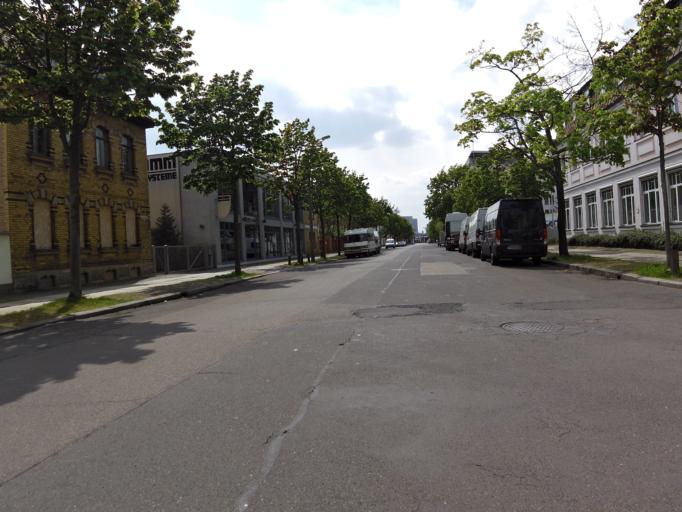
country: DE
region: Saxony
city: Leipzig
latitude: 51.3597
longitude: 12.3906
